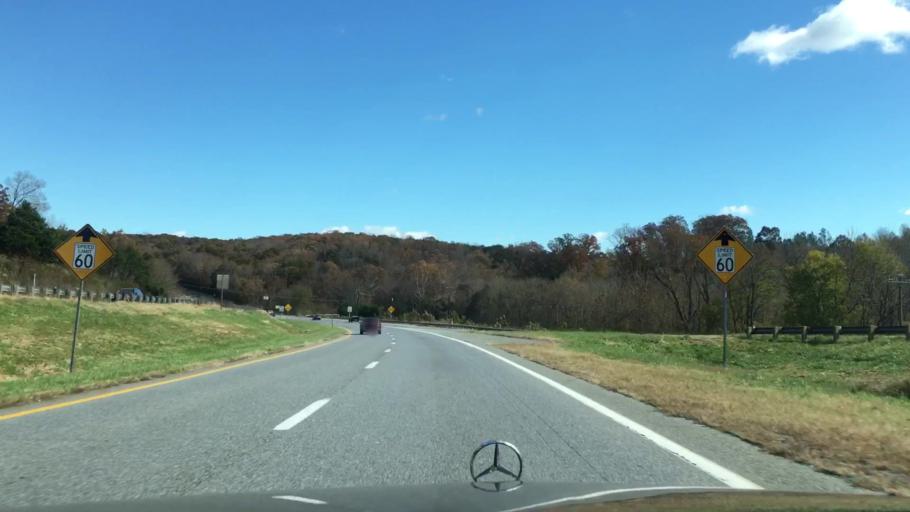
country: US
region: Virginia
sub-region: Campbell County
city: Altavista
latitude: 37.1382
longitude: -79.2485
